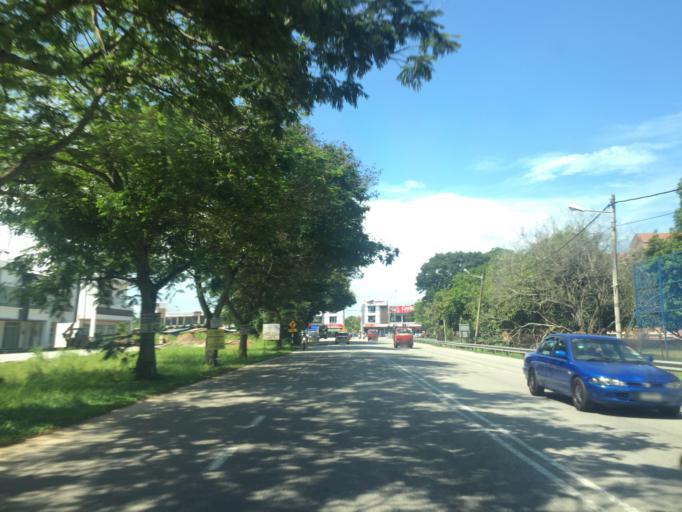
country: MY
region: Penang
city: Tasek Glugor
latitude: 5.4889
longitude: 100.4590
